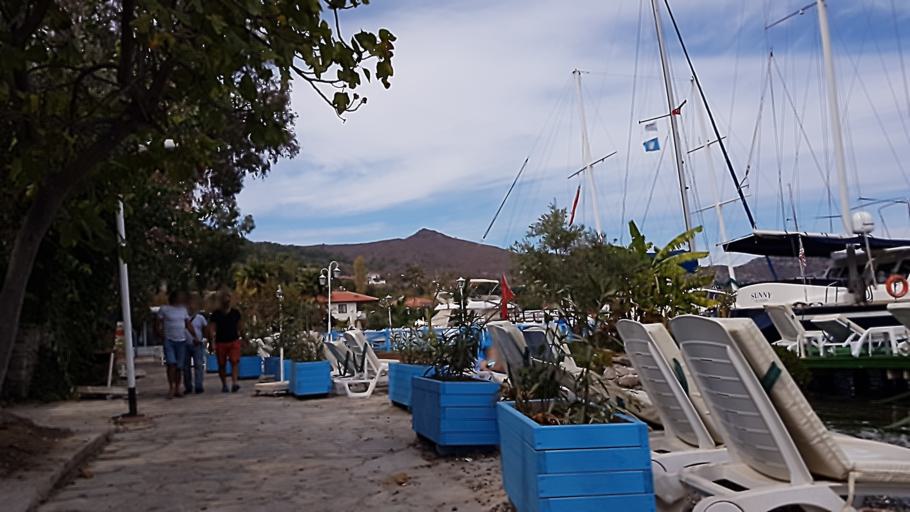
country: TR
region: Mugla
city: Bozburun
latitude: 36.7074
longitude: 28.0905
